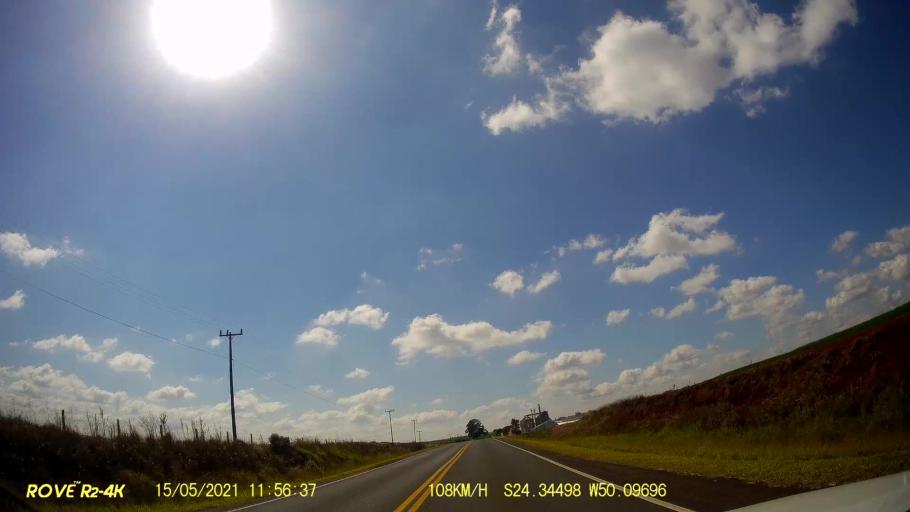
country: BR
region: Parana
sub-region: Pirai Do Sul
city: Pirai do Sul
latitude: -24.3450
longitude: -50.0970
